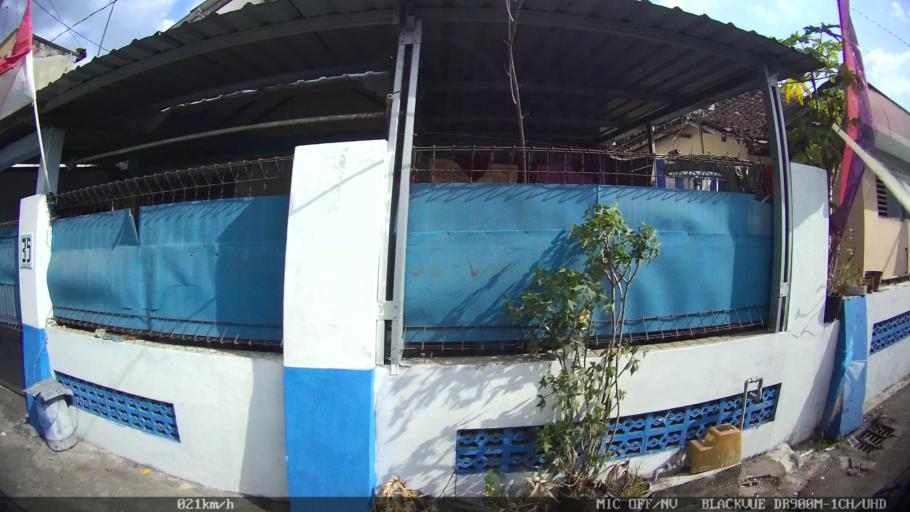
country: ID
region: Daerah Istimewa Yogyakarta
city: Gamping Lor
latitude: -7.7930
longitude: 110.3447
